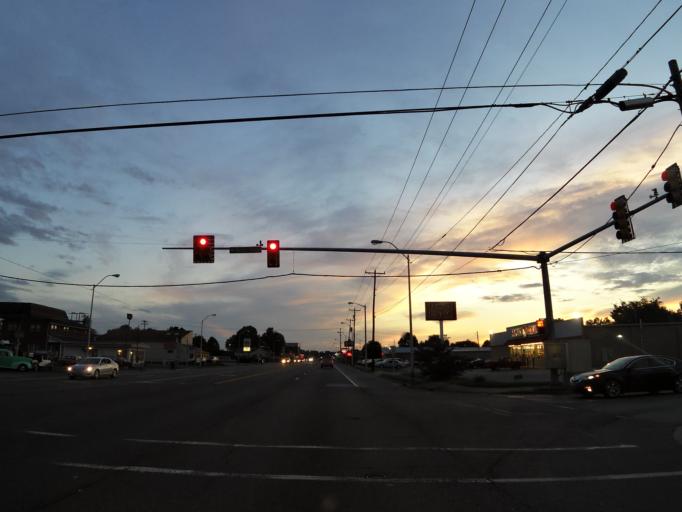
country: US
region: Tennessee
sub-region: Carter County
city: Elizabethton
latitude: 36.3516
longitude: -82.2154
